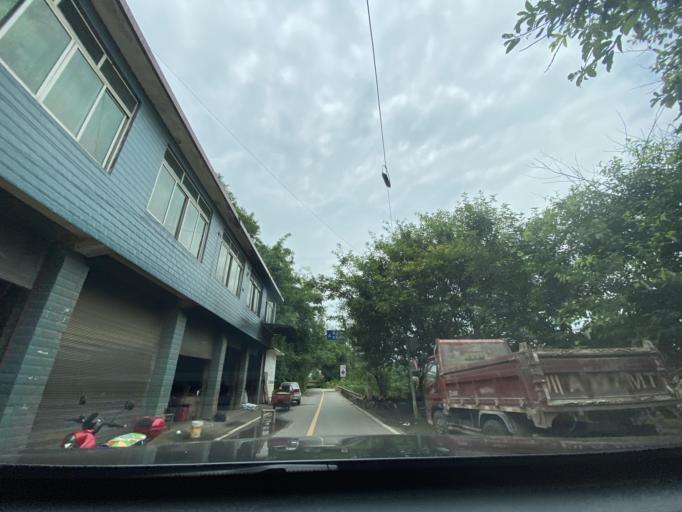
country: CN
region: Sichuan
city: Wujin
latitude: 30.3708
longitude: 103.9694
